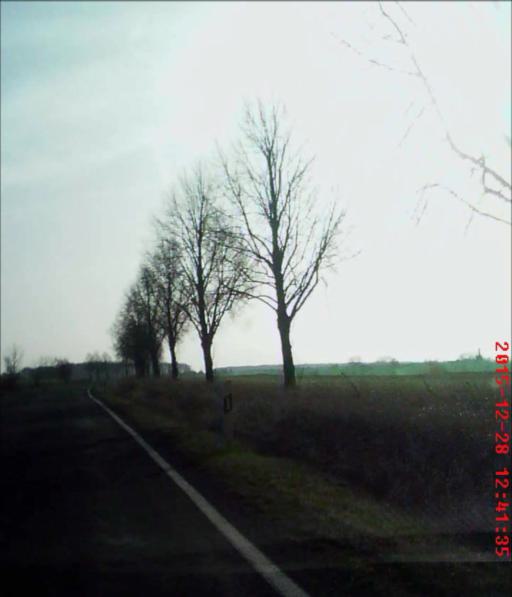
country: DE
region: Thuringia
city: Wiegendorf
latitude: 50.9994
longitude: 11.4289
